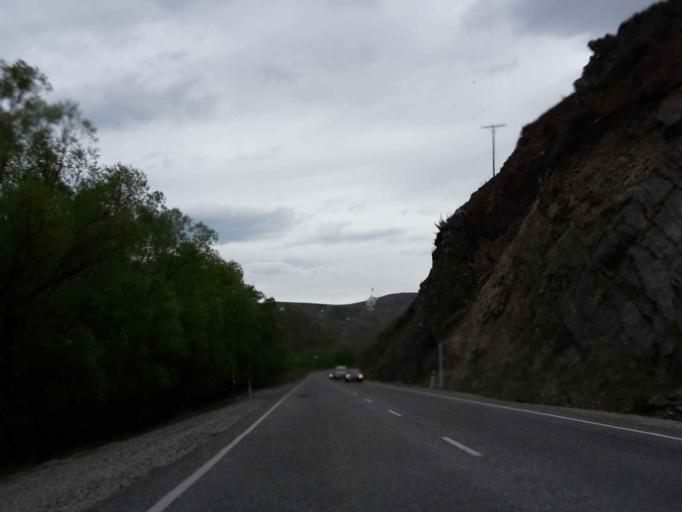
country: NZ
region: Otago
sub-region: Queenstown-Lakes District
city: Wanaka
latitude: -44.6861
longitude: 169.4857
